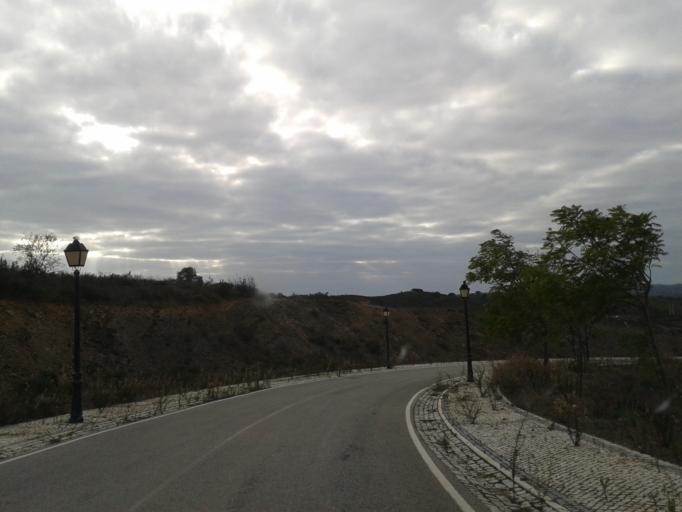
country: PT
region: Faro
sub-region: Castro Marim
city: Castro Marim
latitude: 37.2534
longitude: -7.4478
